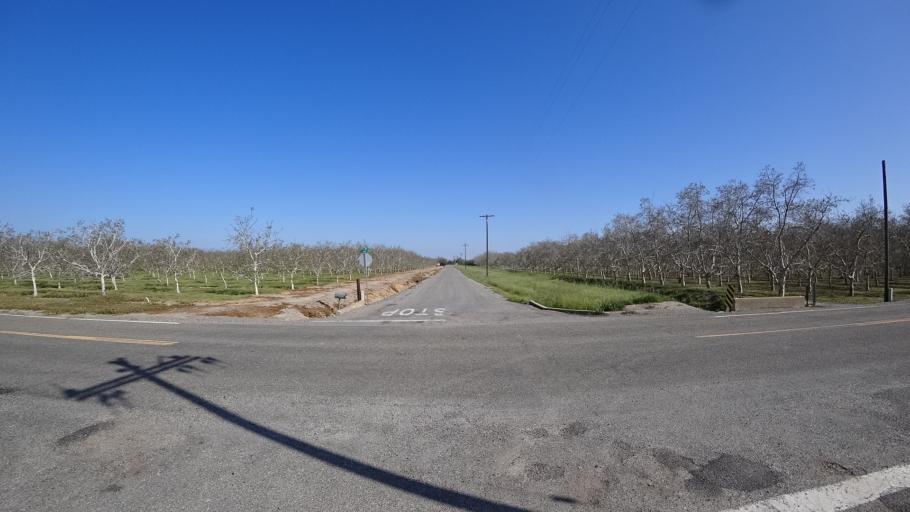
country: US
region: California
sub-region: Glenn County
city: Hamilton City
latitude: 39.6305
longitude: -122.0275
